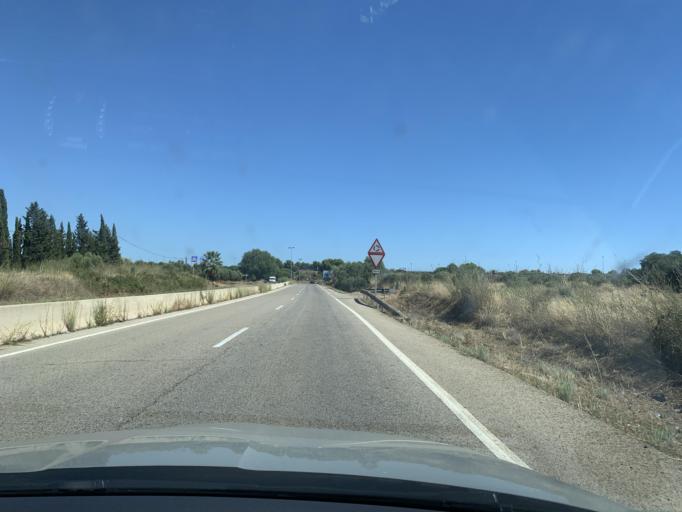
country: ES
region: Catalonia
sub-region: Provincia de Tarragona
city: Vila-seca
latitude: 41.1351
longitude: 1.1389
